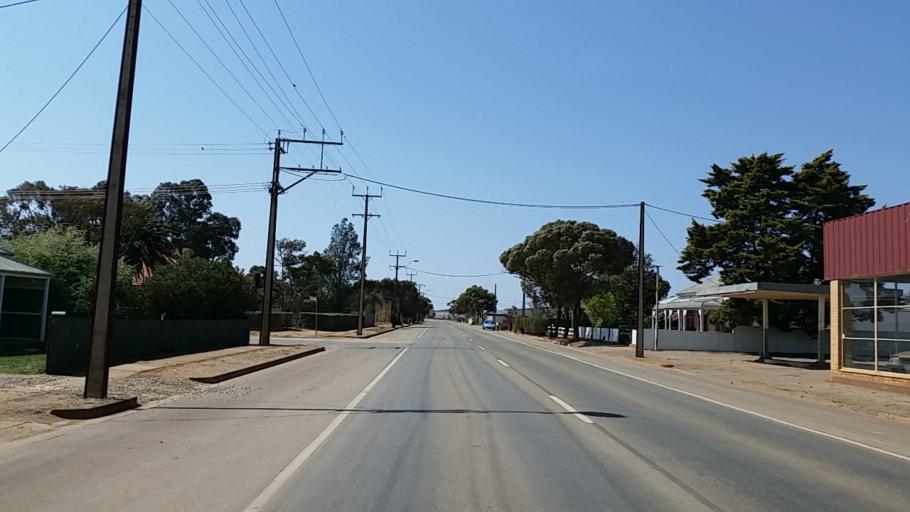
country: AU
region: South Australia
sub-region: Peterborough
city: Peterborough
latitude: -32.9728
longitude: 138.8435
